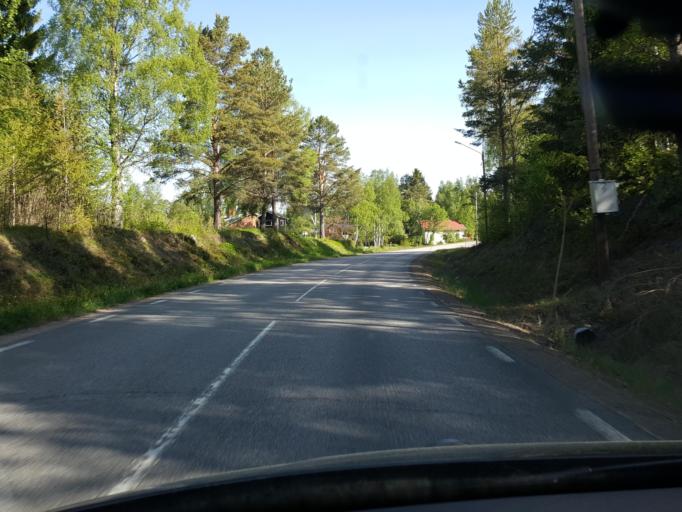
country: SE
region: Vaesternorrland
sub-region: Ange Kommun
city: Ange
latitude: 62.1814
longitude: 15.6523
